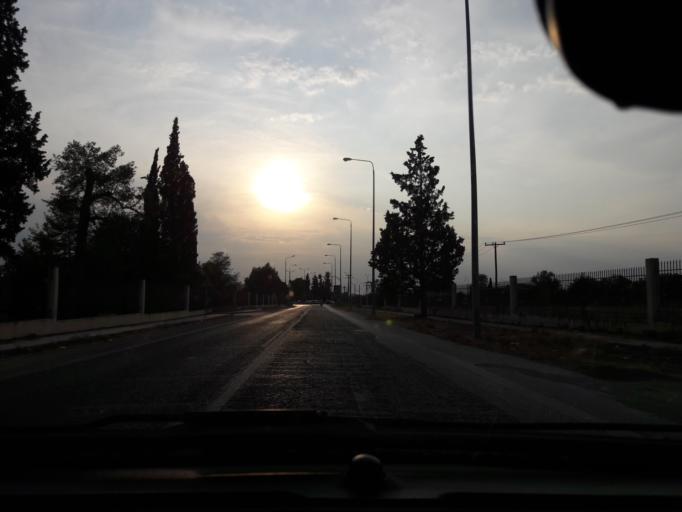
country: GR
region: Central Macedonia
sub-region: Nomos Thessalonikis
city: Thermi
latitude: 40.5390
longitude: 22.9937
